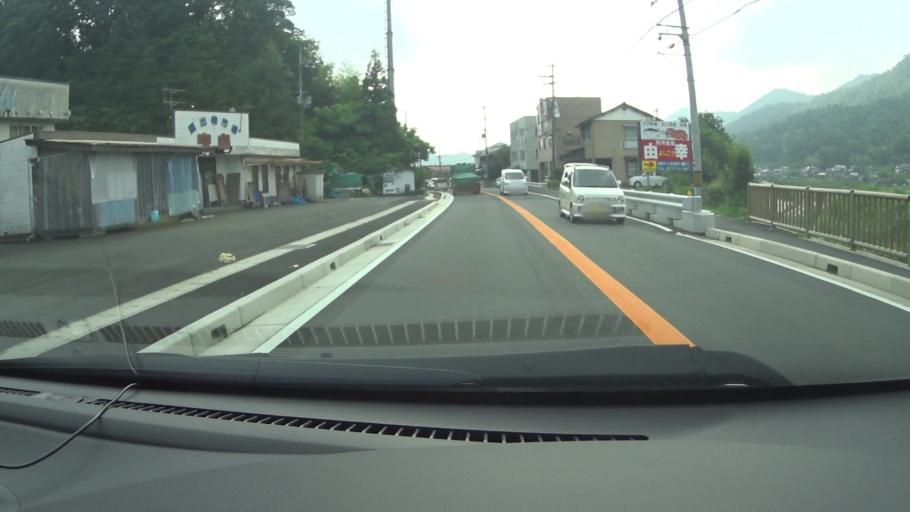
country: JP
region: Kyoto
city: Maizuru
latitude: 35.4809
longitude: 135.4330
